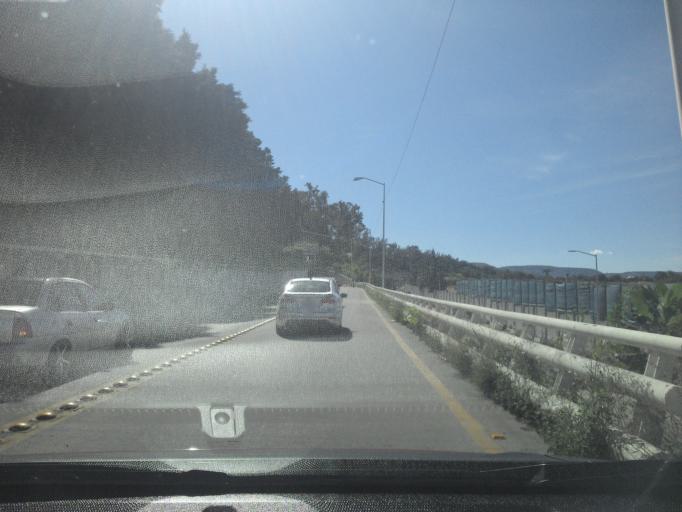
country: MX
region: Jalisco
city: Zapopan2
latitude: 20.7173
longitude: -103.4277
